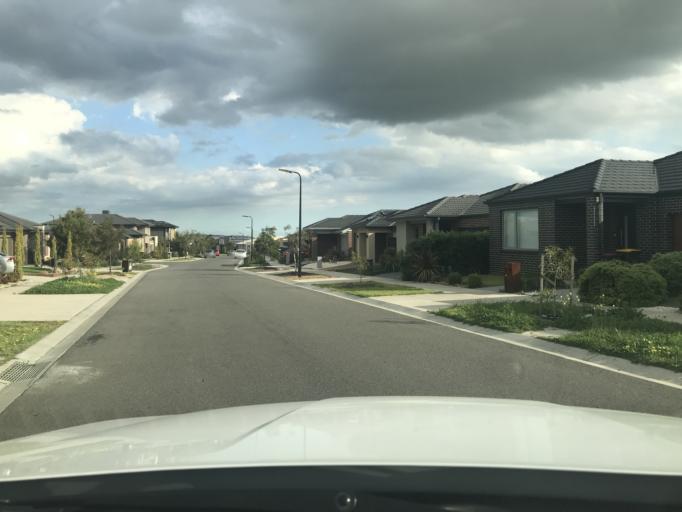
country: AU
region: Victoria
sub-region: Hume
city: Craigieburn
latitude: -37.5774
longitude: 144.9028
